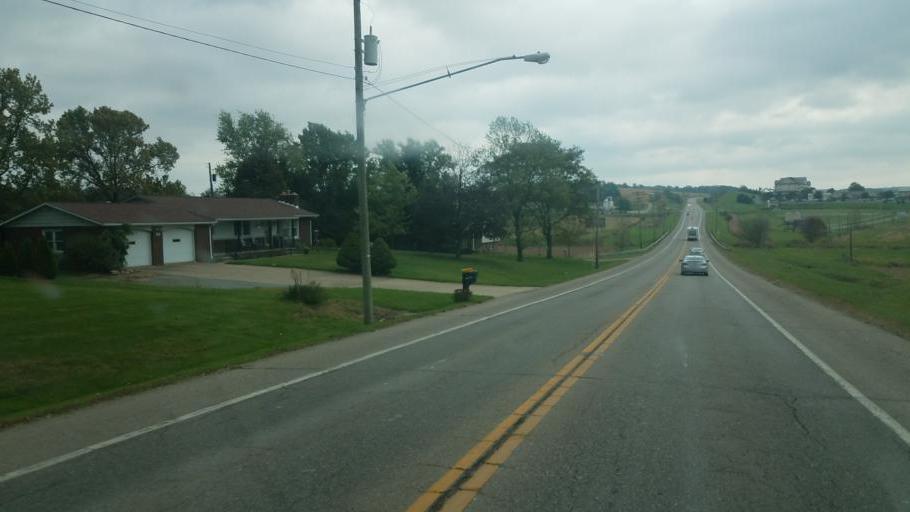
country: US
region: Ohio
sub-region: Tuscarawas County
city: Sugarcreek
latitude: 40.5089
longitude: -81.6171
